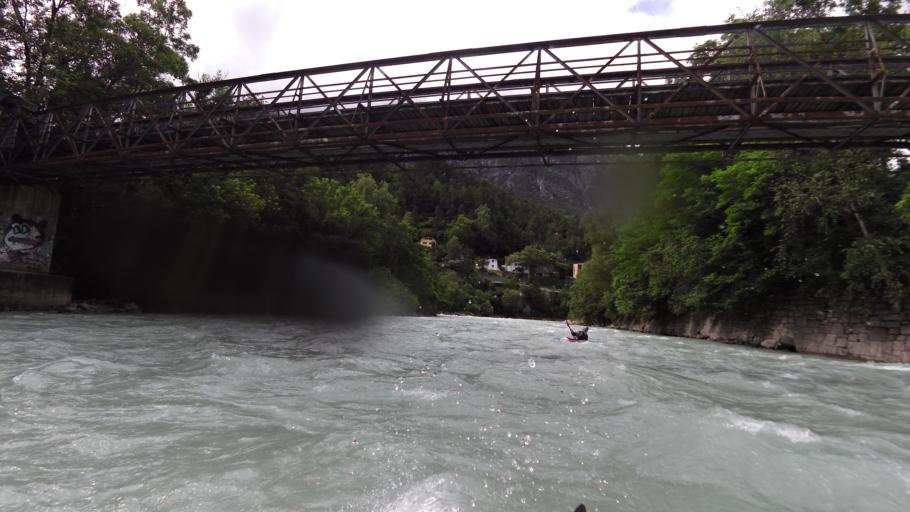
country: AT
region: Tyrol
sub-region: Politischer Bezirk Landeck
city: Landeck
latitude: 47.1425
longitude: 10.5652
